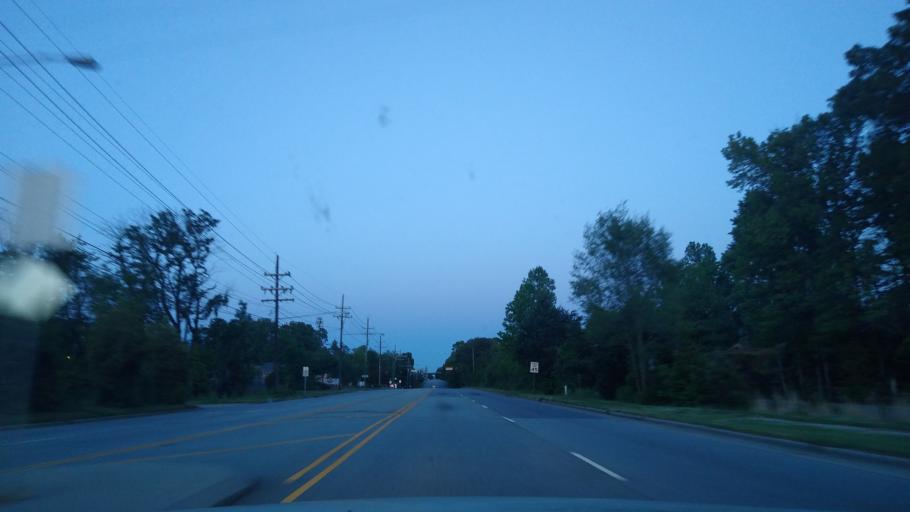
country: US
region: North Carolina
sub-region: Guilford County
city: Oak Ridge
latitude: 36.0936
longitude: -79.9634
